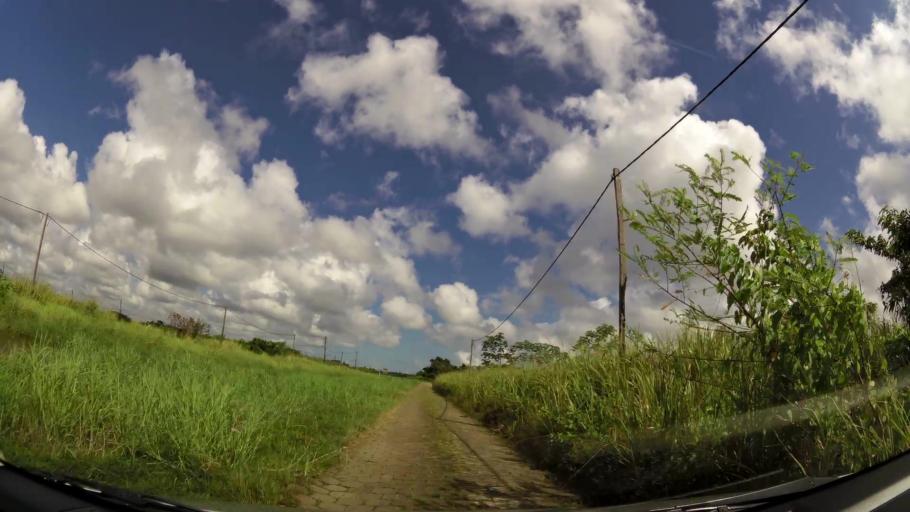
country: SR
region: Paramaribo
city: Paramaribo
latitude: 5.8697
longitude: -55.1258
